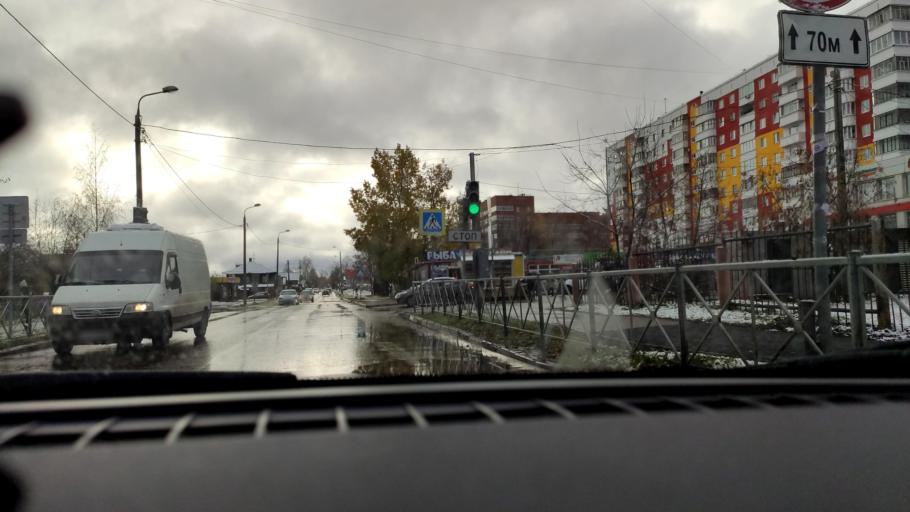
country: RU
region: Perm
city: Perm
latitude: 58.0329
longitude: 56.3250
